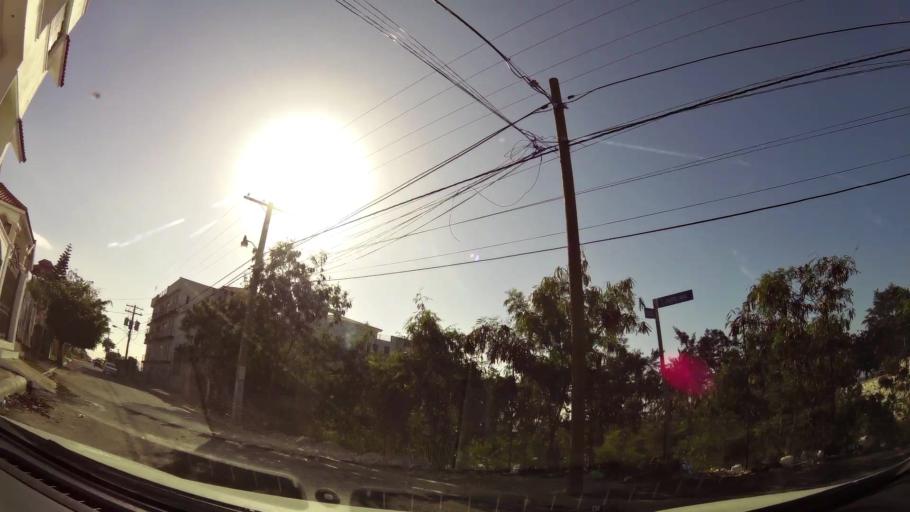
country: DO
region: Santo Domingo
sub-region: Santo Domingo
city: Santo Domingo Este
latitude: 18.4698
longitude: -69.8607
